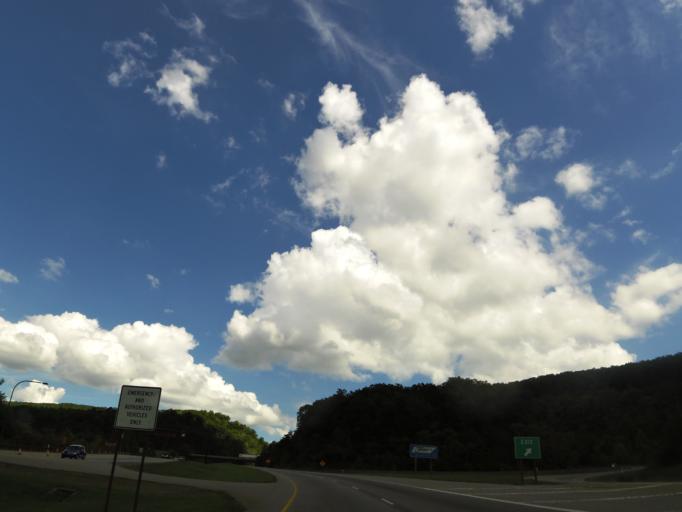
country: US
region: Tennessee
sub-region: Claiborne County
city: Harrogate
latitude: 36.5930
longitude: -83.6679
